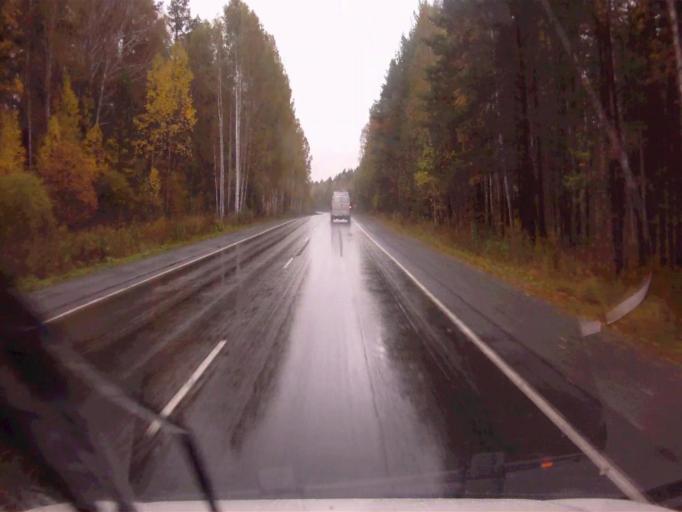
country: RU
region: Chelyabinsk
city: Tayginka
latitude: 55.5655
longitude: 60.6497
